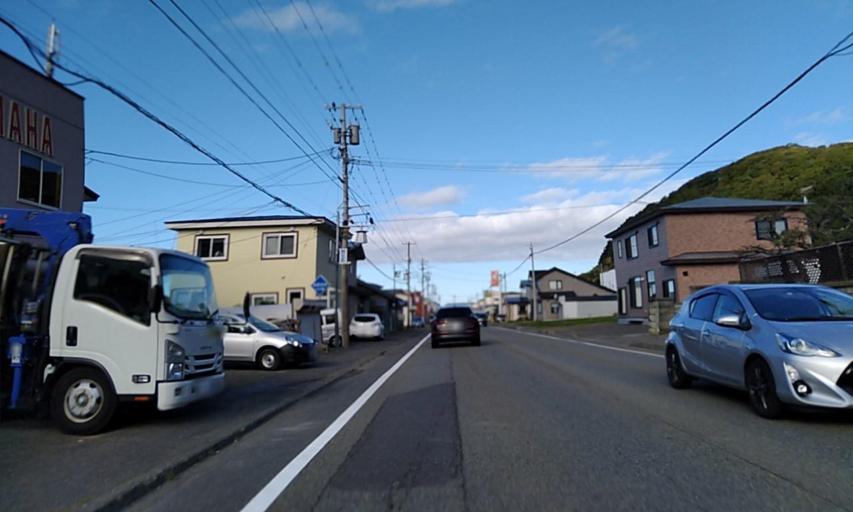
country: JP
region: Hokkaido
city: Shizunai-furukawacho
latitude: 42.2509
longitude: 142.5479
